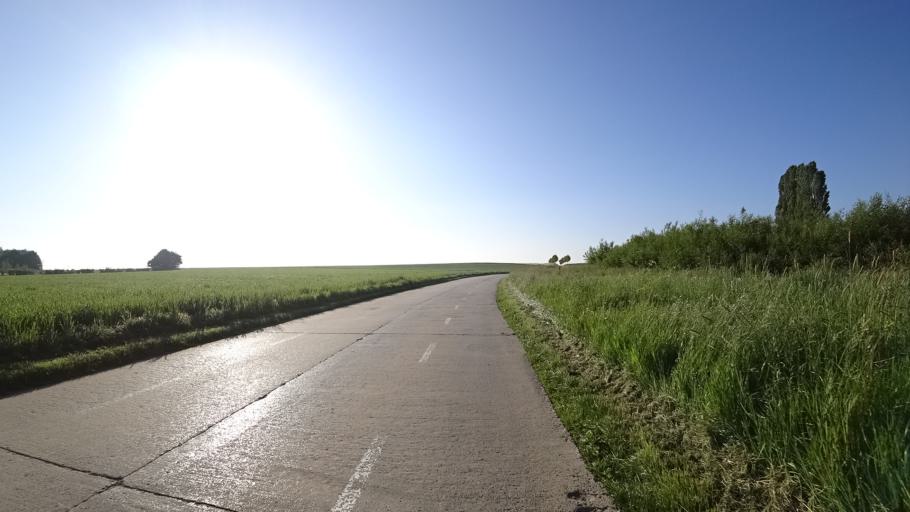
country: BE
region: Wallonia
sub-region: Province du Brabant Wallon
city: Walhain-Saint-Paul
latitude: 50.6369
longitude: 4.6766
